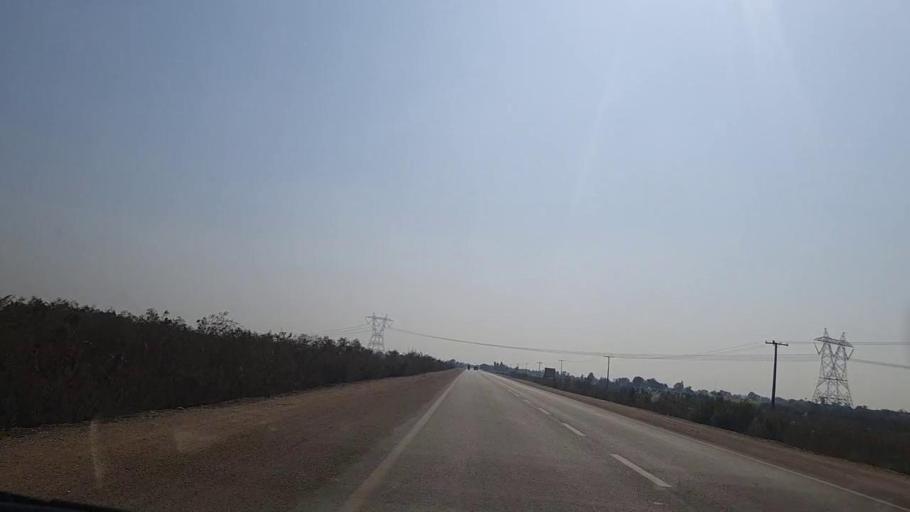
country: PK
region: Sindh
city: Sakrand
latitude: 26.0064
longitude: 68.3937
